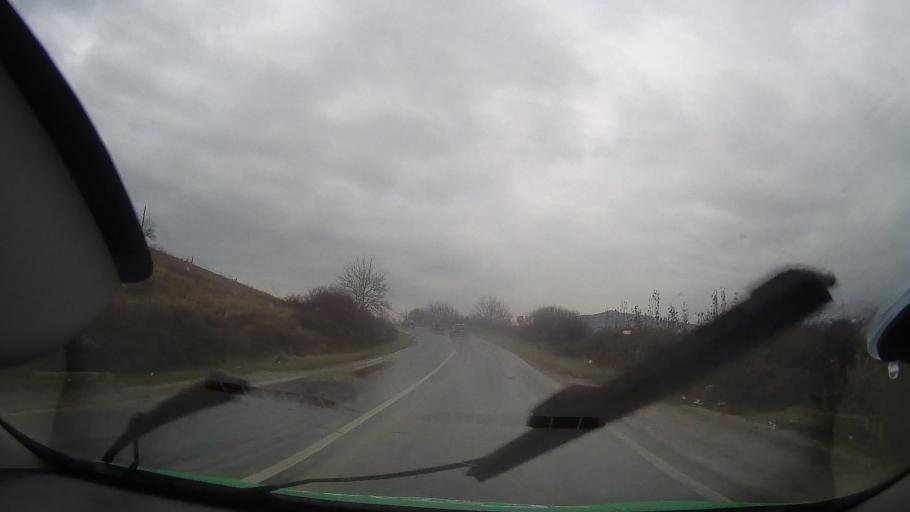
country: RO
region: Bihor
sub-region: Comuna Rabagani
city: Rabagani
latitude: 46.7551
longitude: 22.2061
